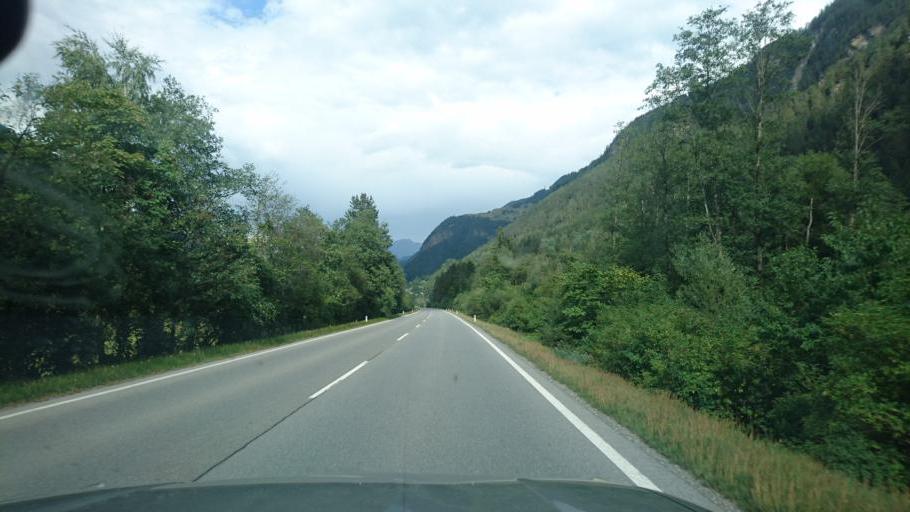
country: AT
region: Tyrol
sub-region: Politischer Bezirk Landeck
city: Serfaus
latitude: 46.9980
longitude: 10.5854
